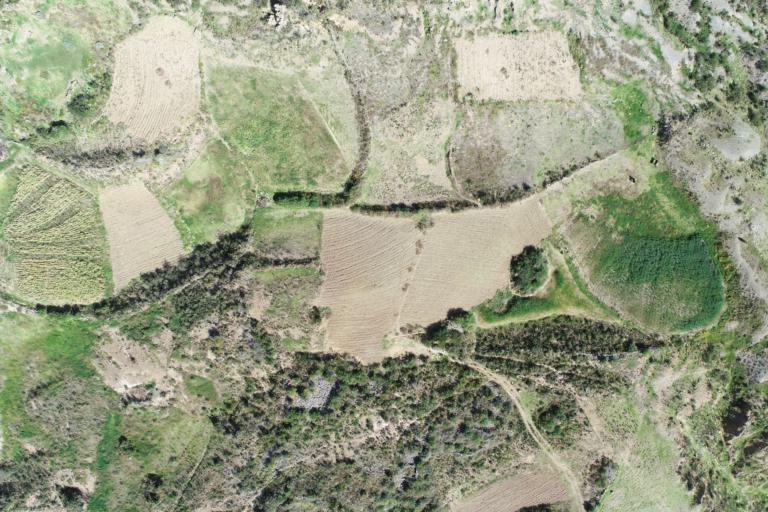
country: BO
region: La Paz
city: La Paz
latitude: -16.5576
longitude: -67.9892
